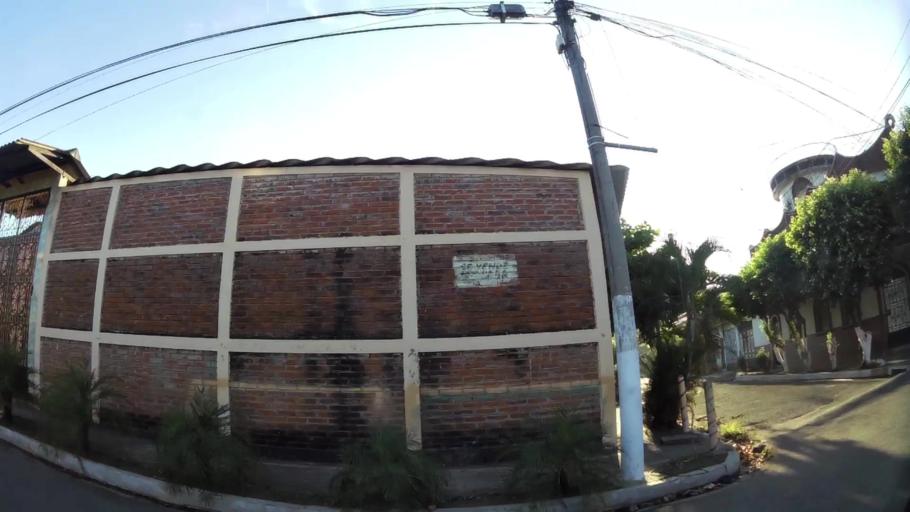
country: SV
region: Sonsonate
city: San Antonio del Monte
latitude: 13.7064
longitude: -89.7341
